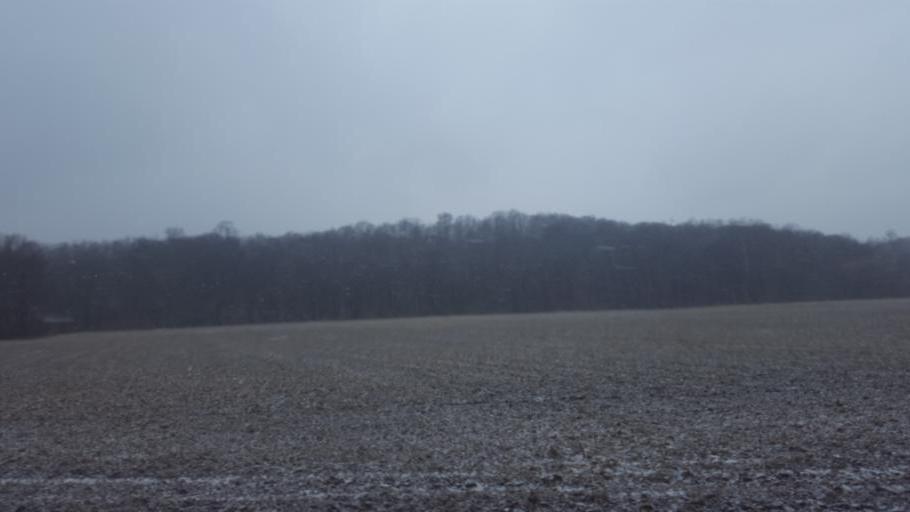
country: US
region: Ohio
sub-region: Coshocton County
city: West Lafayette
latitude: 40.3350
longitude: -81.7447
